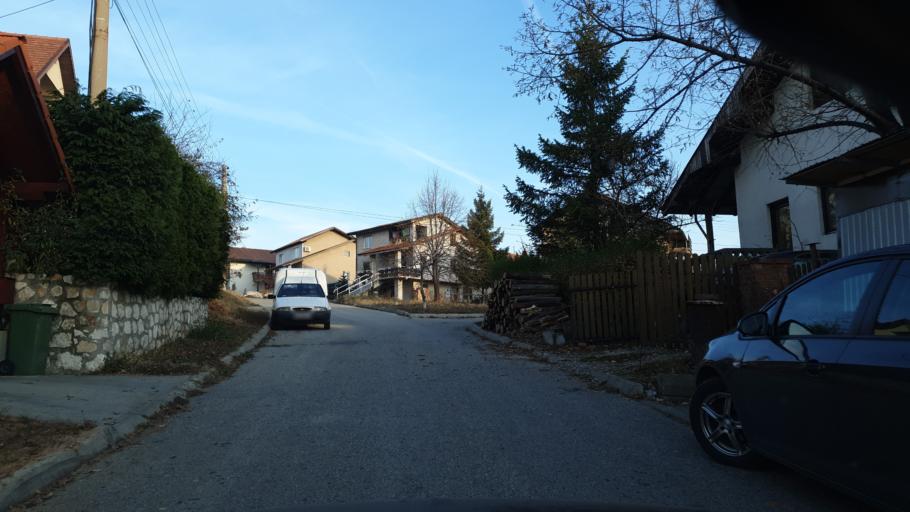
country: RS
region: Central Serbia
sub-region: Borski Okrug
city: Bor
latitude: 44.0578
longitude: 22.0812
